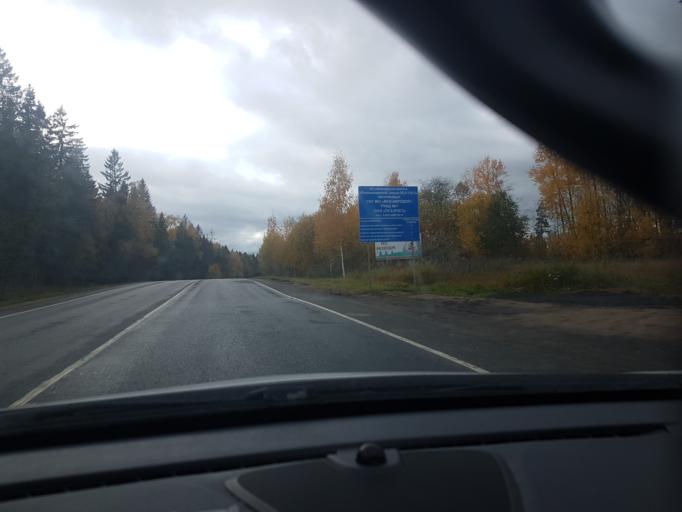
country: RU
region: Moskovskaya
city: Sychevo
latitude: 56.0044
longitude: 36.2982
